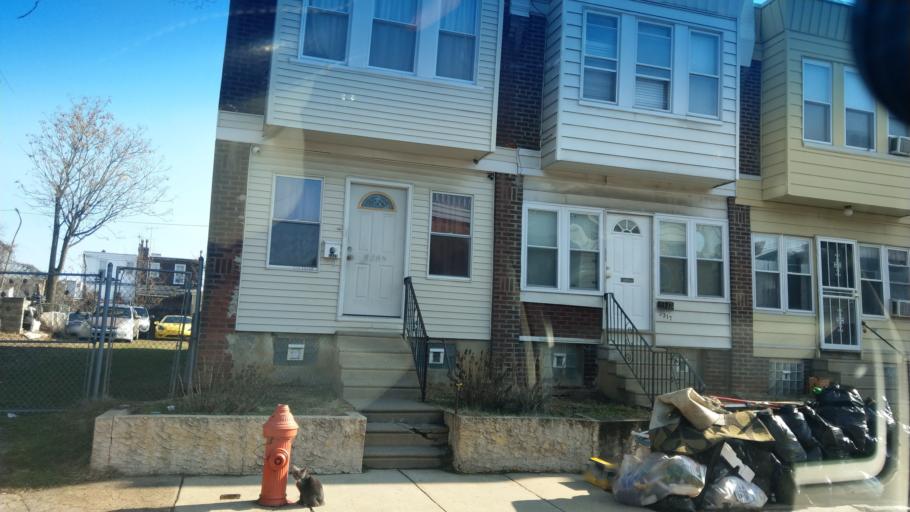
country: US
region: Pennsylvania
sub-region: Montgomery County
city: Rockledge
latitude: 40.0318
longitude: -75.1274
